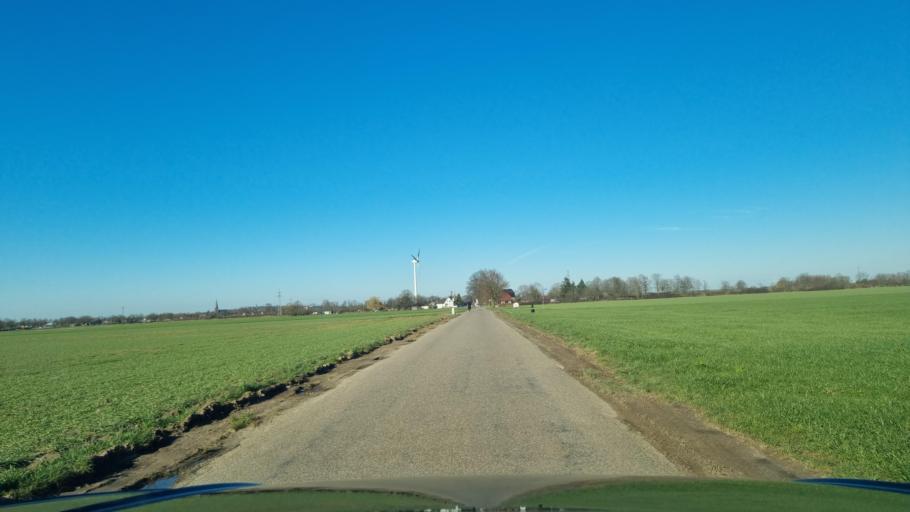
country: DE
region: North Rhine-Westphalia
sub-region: Regierungsbezirk Dusseldorf
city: Kleve
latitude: 51.8074
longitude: 6.1689
